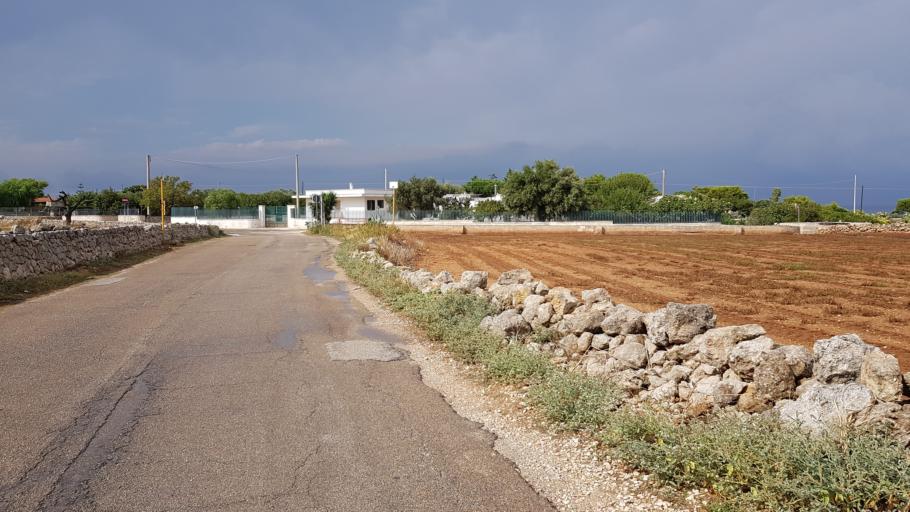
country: IT
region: Apulia
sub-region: Provincia di Bari
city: Monopoli
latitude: 40.9288
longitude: 17.3284
